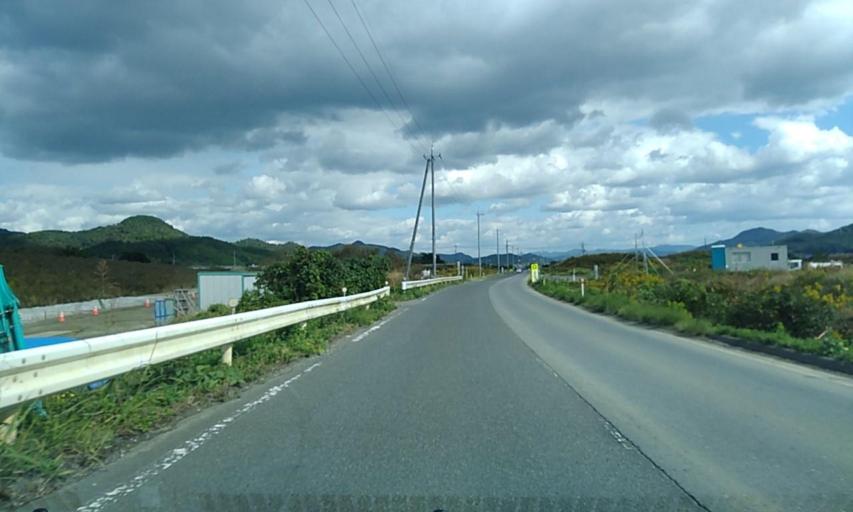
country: JP
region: Kyoto
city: Fukuchiyama
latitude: 35.3039
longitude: 135.1571
